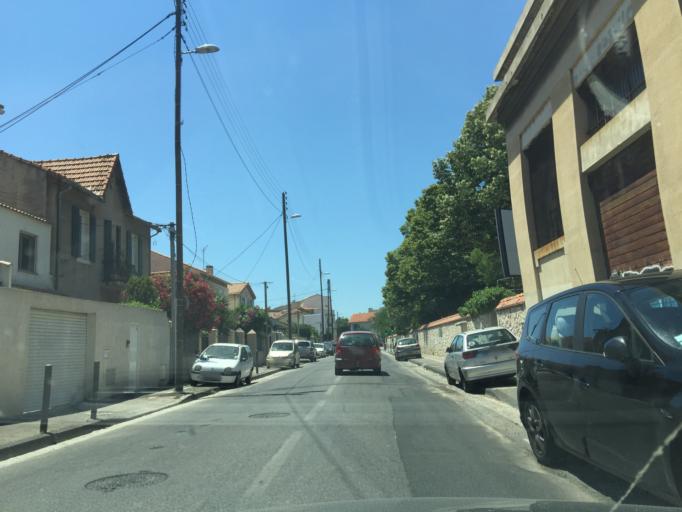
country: FR
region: Provence-Alpes-Cote d'Azur
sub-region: Departement des Bouches-du-Rhone
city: Marseille 08
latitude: 43.2638
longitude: 5.3895
